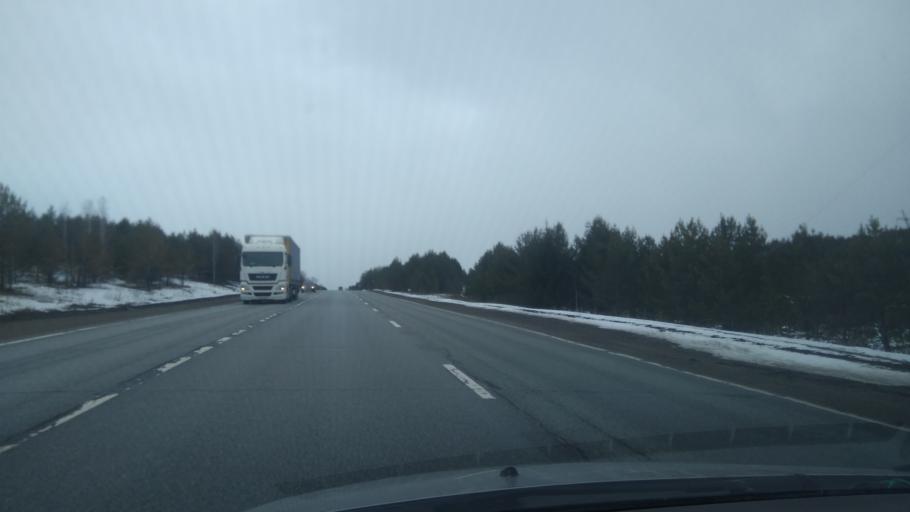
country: RU
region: Sverdlovsk
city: Achit
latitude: 56.8791
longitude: 57.6343
